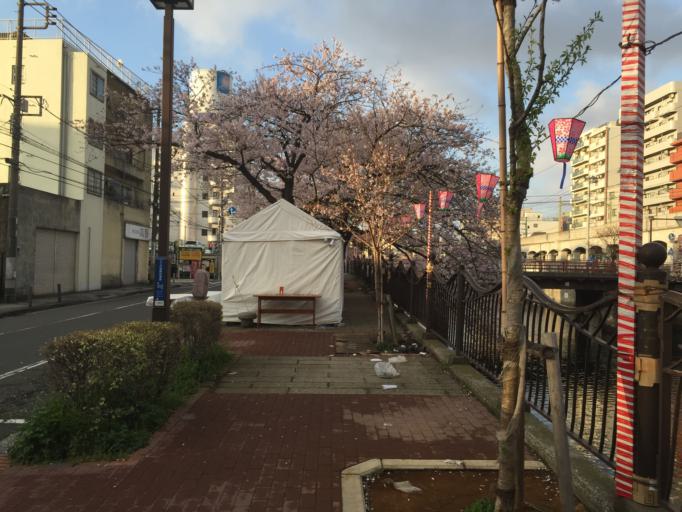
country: JP
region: Kanagawa
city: Yokohama
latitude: 35.4440
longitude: 139.6274
